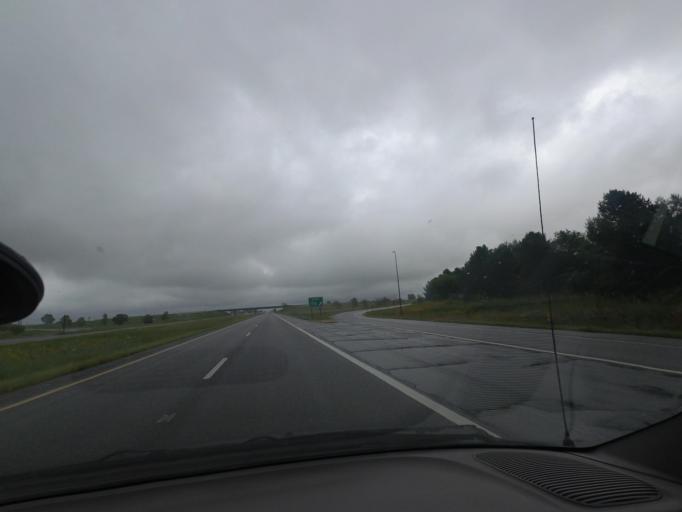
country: US
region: Illinois
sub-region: Champaign County
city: Mahomet
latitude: 40.1203
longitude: -88.4116
